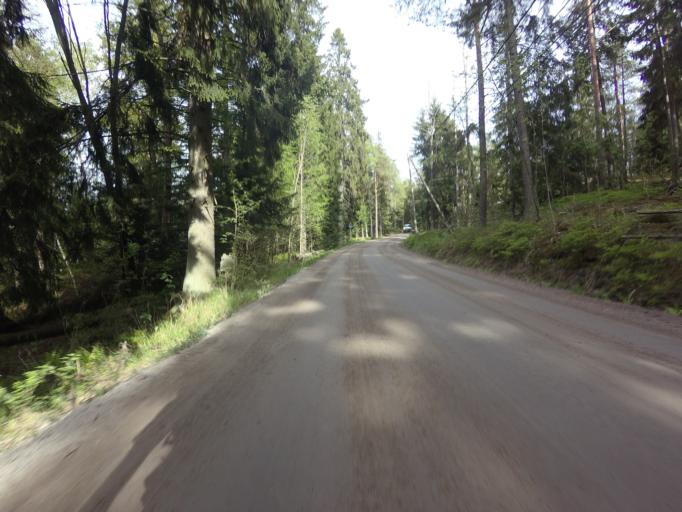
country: FI
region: Uusimaa
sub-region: Helsinki
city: Koukkuniemi
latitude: 60.1170
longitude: 24.7213
